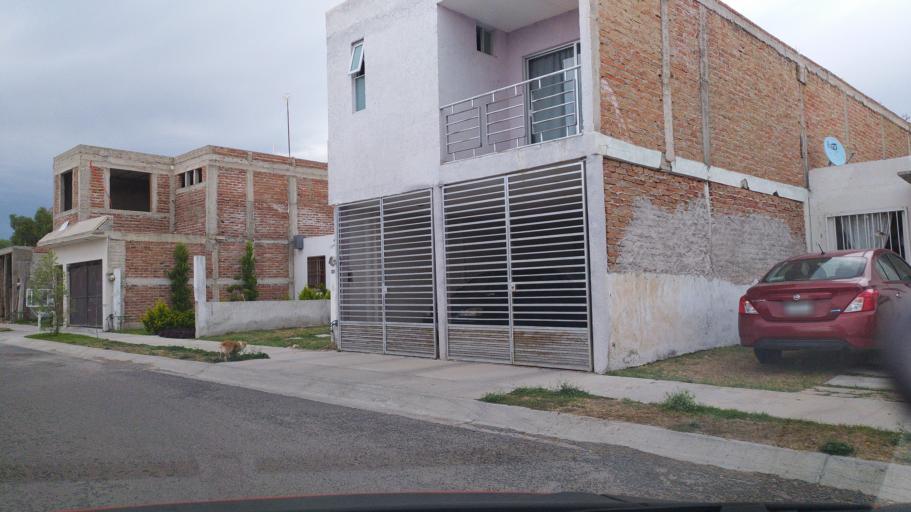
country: MX
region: Guanajuato
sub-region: San Francisco del Rincon
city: Estacion de San Francisco
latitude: 21.0307
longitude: -101.8280
